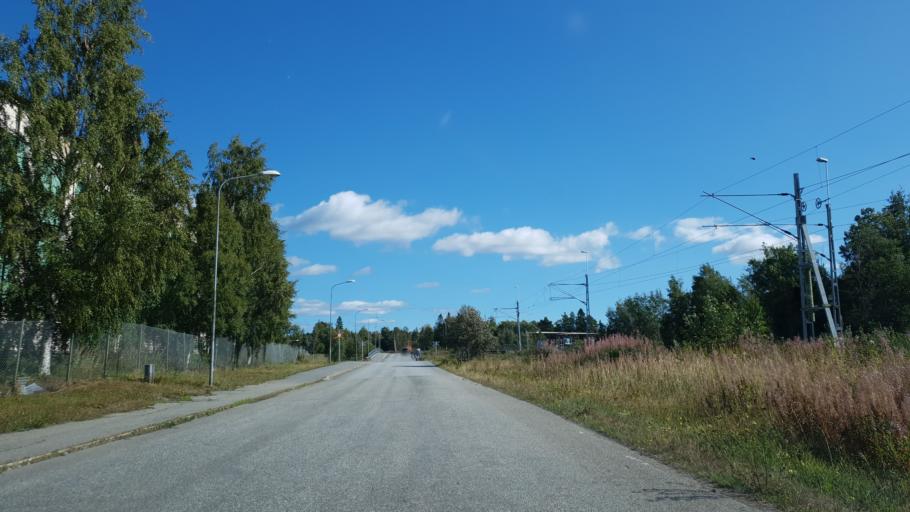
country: SE
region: Vaesterbotten
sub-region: Umea Kommun
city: Holmsund
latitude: 63.7040
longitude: 20.3580
